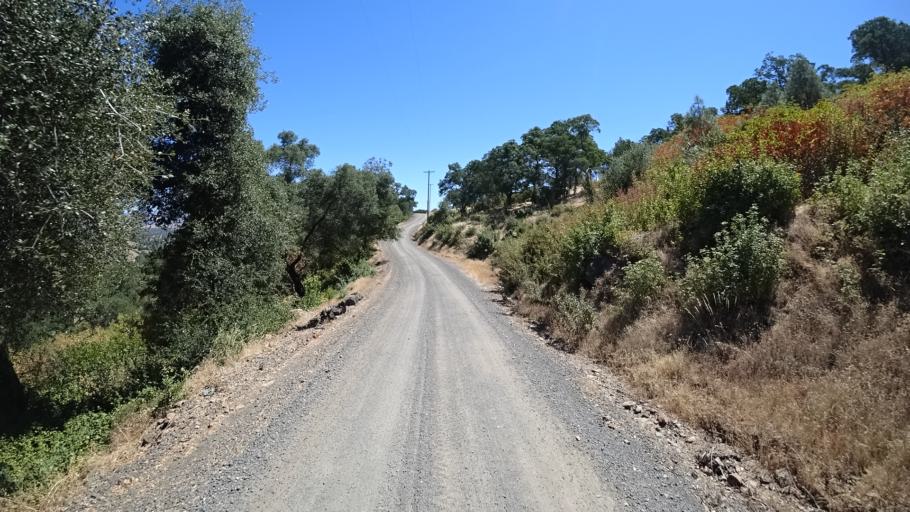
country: US
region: California
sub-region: Calaveras County
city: Copperopolis
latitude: 37.9448
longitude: -120.6976
